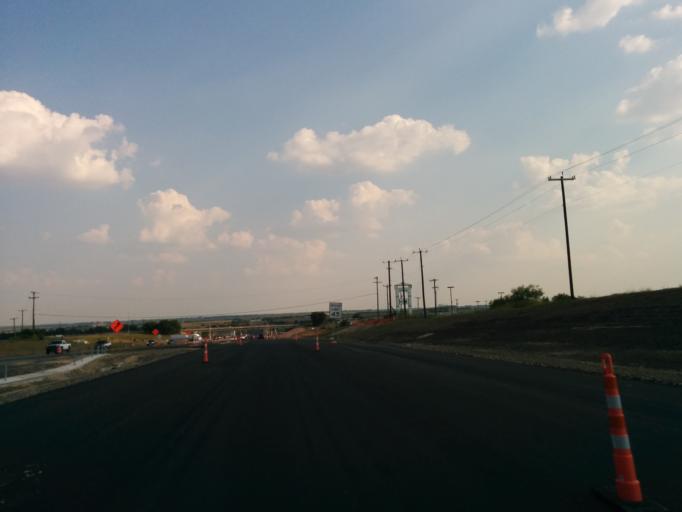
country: US
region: Texas
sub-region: Bexar County
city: Converse
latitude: 29.4691
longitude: -98.2936
